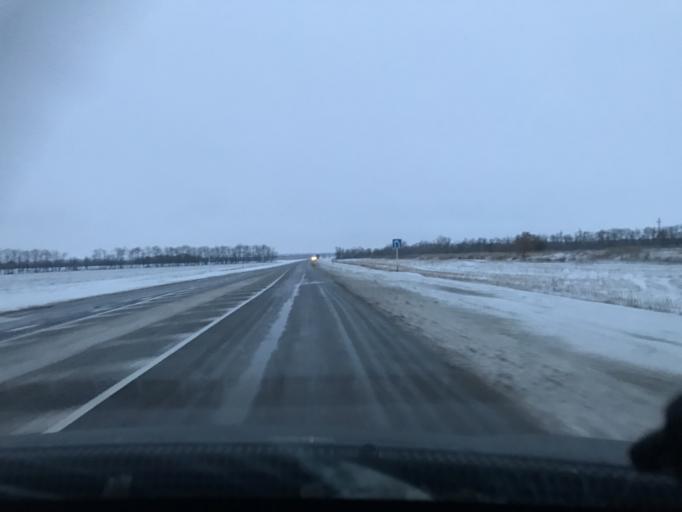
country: RU
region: Rostov
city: Letnik
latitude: 45.9740
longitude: 41.2521
